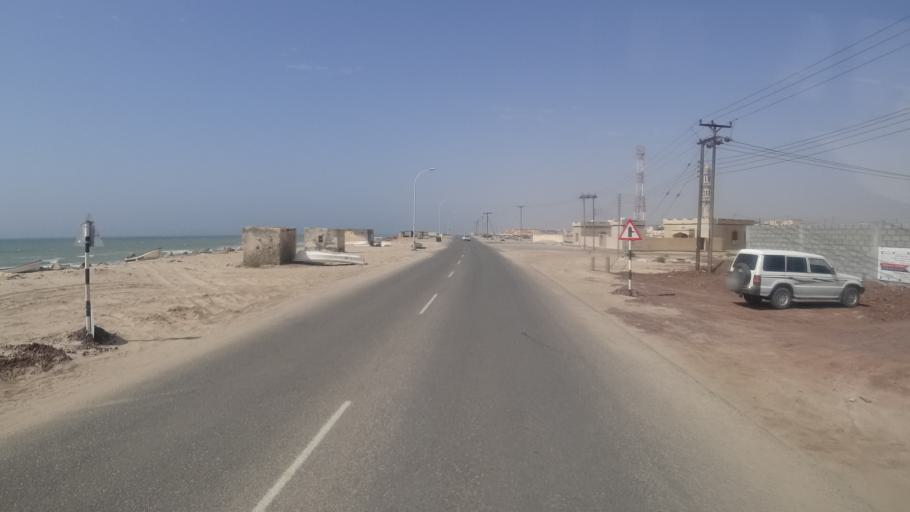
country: OM
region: Ash Sharqiyah
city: Sur
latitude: 22.1249
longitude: 59.7213
